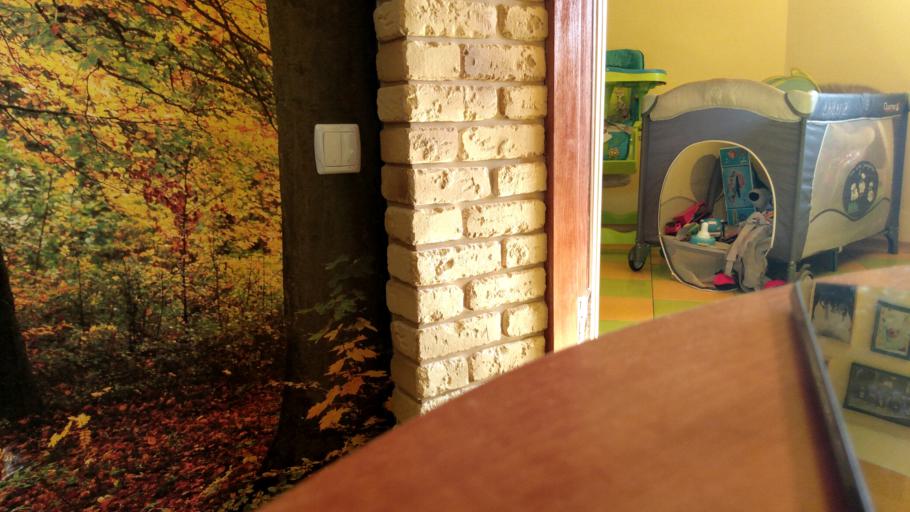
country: RU
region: Tverskaya
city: Radchenko
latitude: 56.7301
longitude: 36.3662
